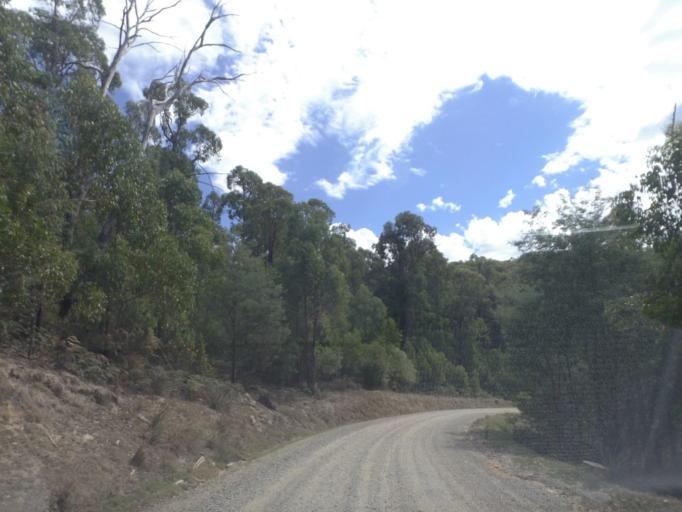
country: AU
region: Victoria
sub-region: Murrindindi
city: Alexandra
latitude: -37.4564
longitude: 145.7563
